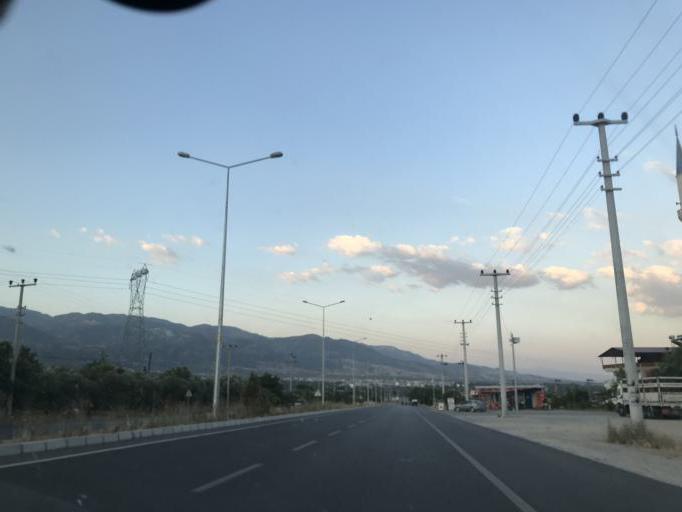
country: TR
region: Aydin
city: Buharkent
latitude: 37.9569
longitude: 28.7073
